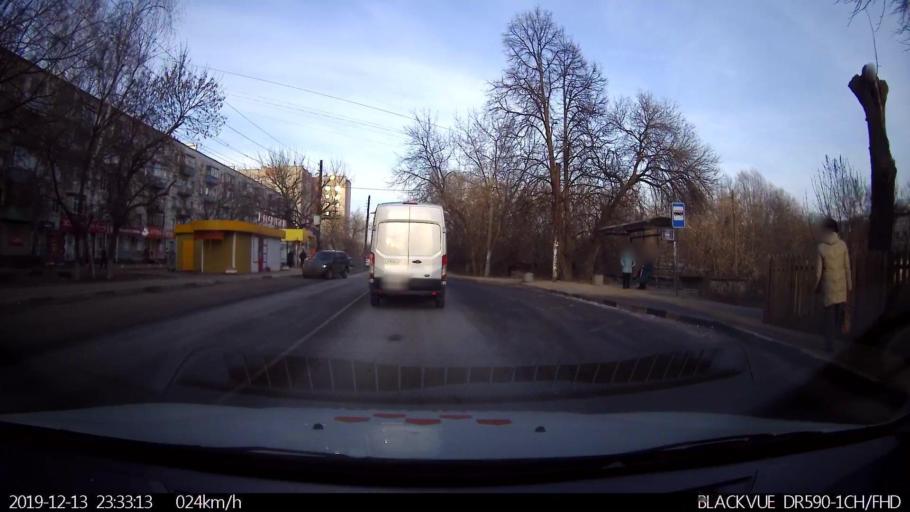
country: RU
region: Nizjnij Novgorod
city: Nizhniy Novgorod
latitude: 56.2789
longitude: 43.9518
